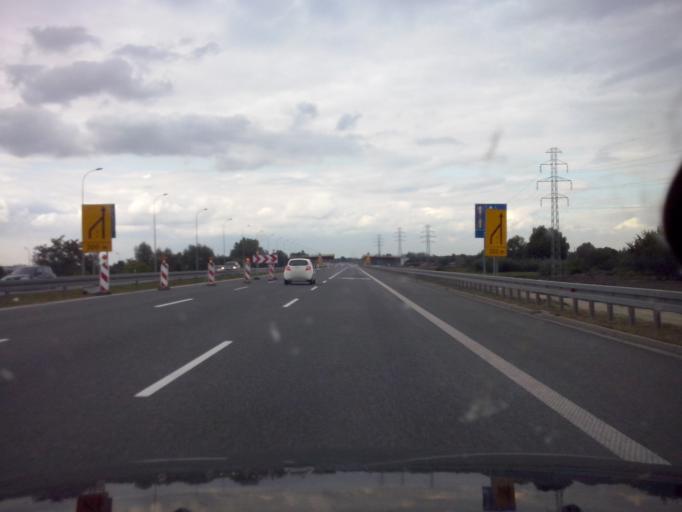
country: PL
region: Lesser Poland Voivodeship
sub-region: Powiat wielicki
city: Kokotow
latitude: 50.0265
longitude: 20.0628
